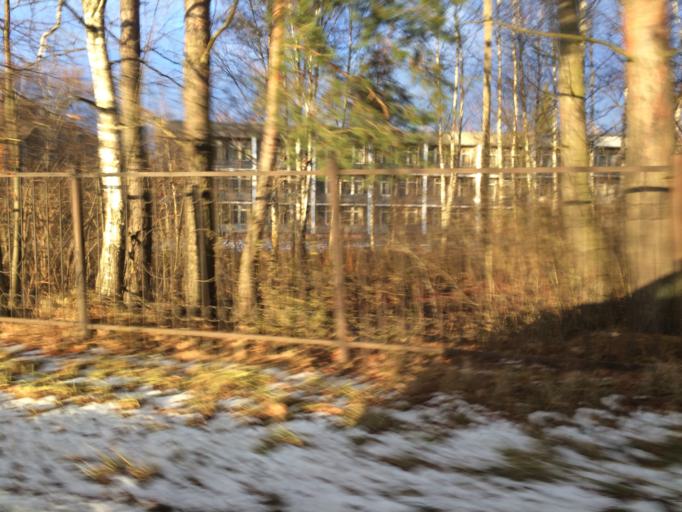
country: RU
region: Tula
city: Cherepet'
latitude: 54.1125
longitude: 36.3339
